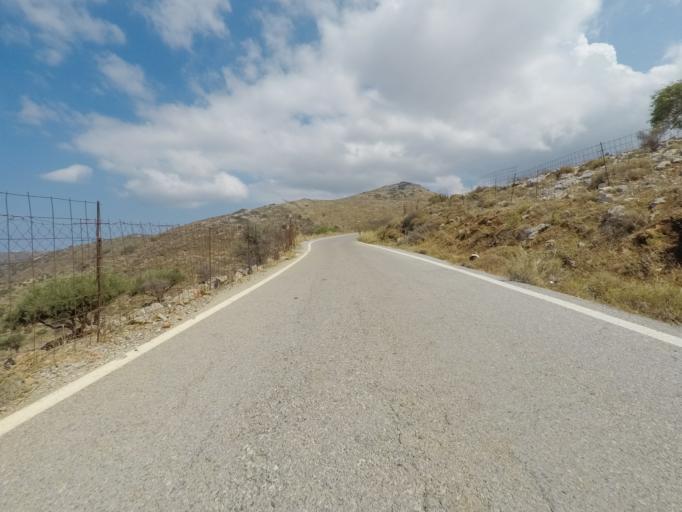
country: GR
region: Crete
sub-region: Nomos Lasithiou
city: Elounda
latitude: 35.3173
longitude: 25.6758
